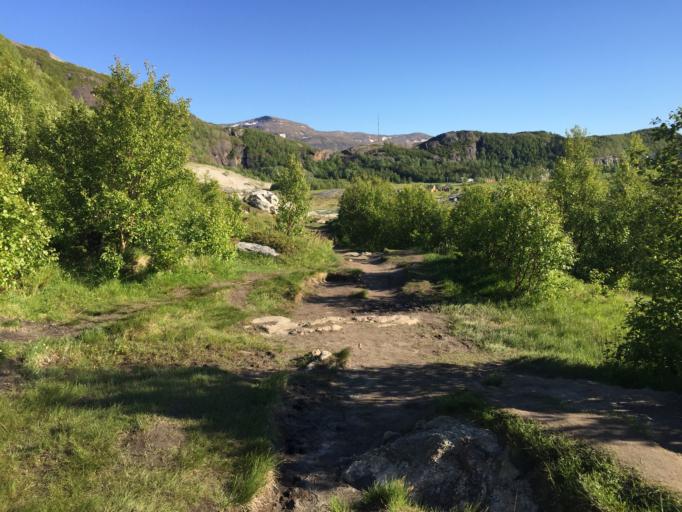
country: NO
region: Nordland
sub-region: Bodo
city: Loding
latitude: 67.4159
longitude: 14.6327
